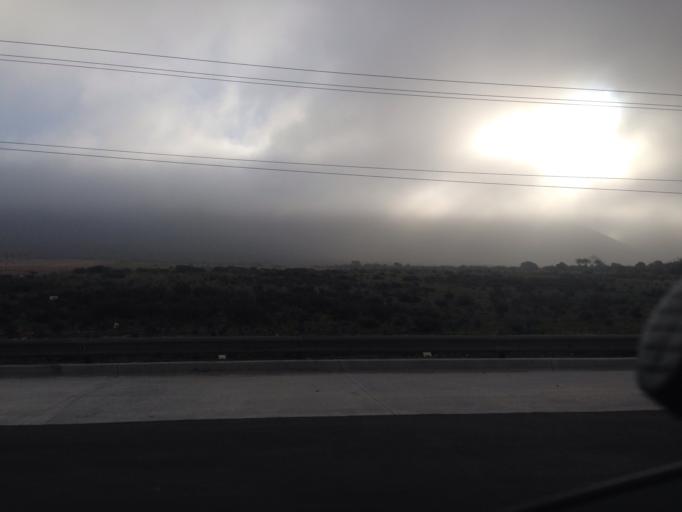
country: MX
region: Baja California
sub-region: Playas de Rosarito
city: Santa Anita
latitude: 32.0664
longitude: -116.8775
